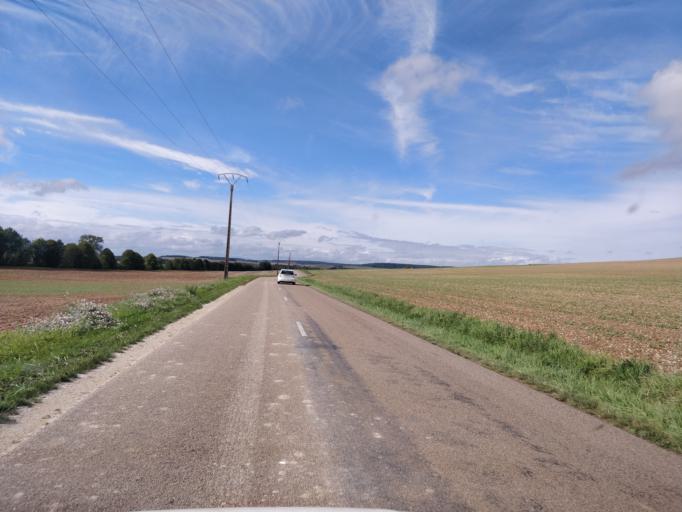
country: FR
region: Champagne-Ardenne
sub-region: Departement de l'Aube
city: Aix-en-Othe
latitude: 48.2148
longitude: 3.6240
